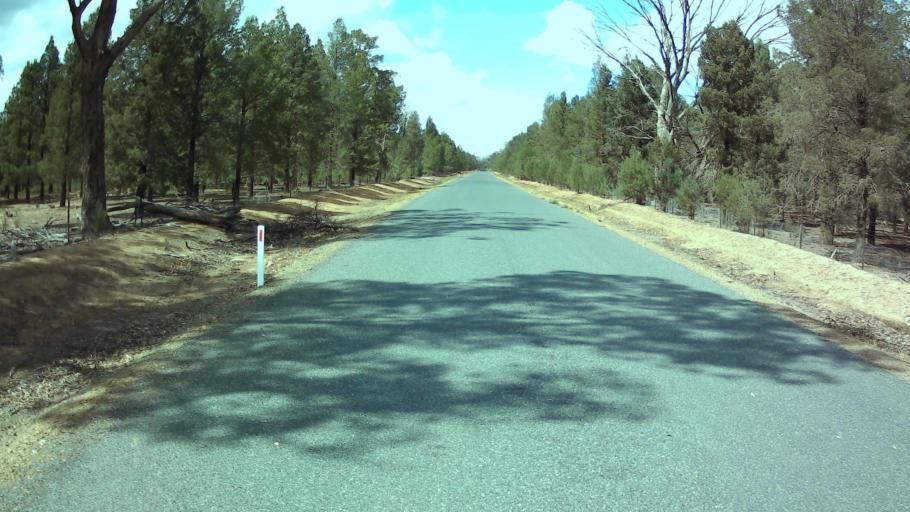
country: AU
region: New South Wales
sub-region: Weddin
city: Grenfell
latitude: -33.8989
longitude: 147.9211
